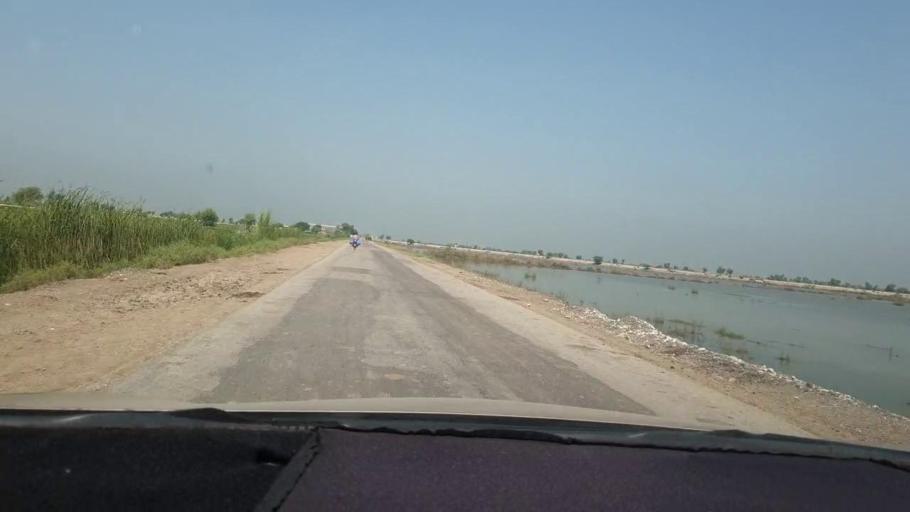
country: PK
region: Sindh
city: Shahdadkot
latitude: 27.8434
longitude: 68.0039
